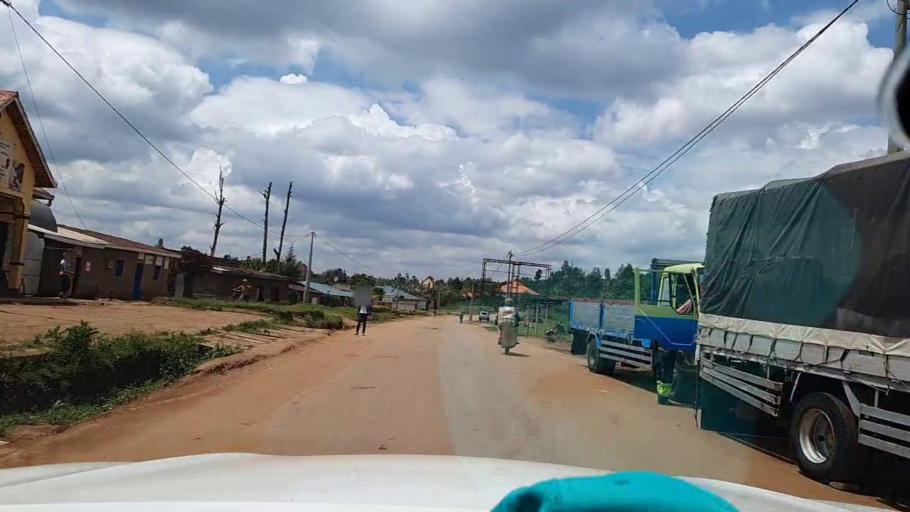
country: RW
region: Southern Province
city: Nzega
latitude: -2.6488
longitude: 29.5604
